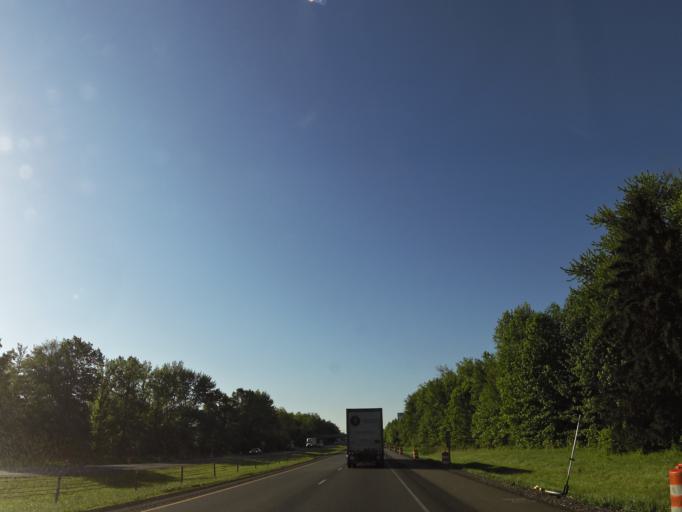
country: US
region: Indiana
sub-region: Jackson County
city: Seymour
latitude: 38.9046
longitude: -85.8236
